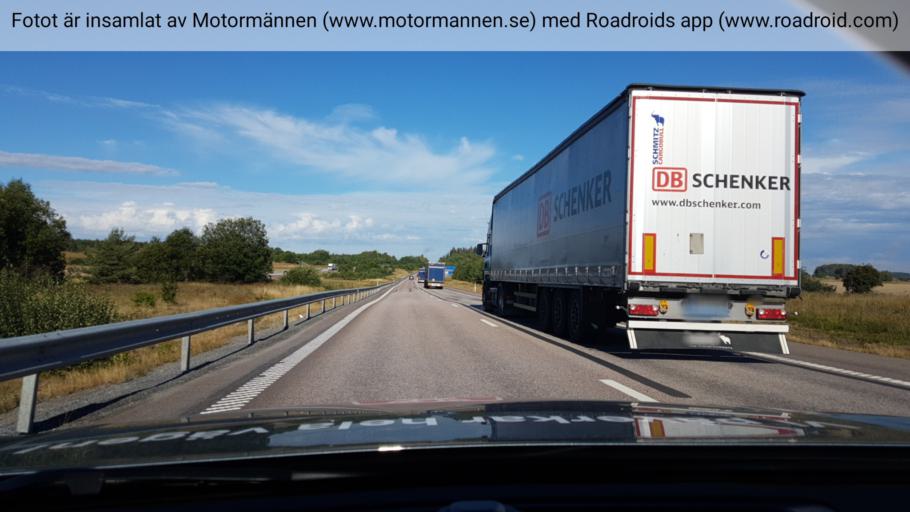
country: SE
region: Uppsala
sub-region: Enkopings Kommun
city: Grillby
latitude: 59.6351
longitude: 17.2855
